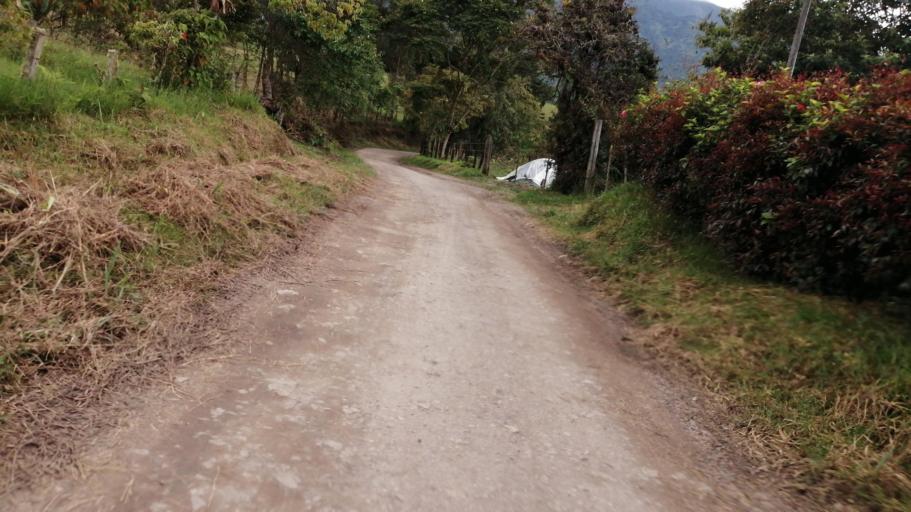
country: CO
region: Boyaca
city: Chinavita
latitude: 5.1357
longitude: -73.3946
